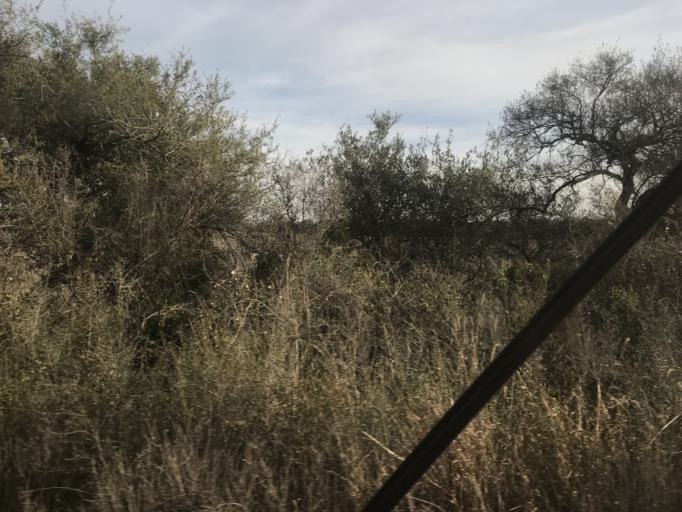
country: AR
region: Cordoba
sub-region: Departamento de Rio Segundo
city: Rio Segundo
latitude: -31.6645
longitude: -63.9010
